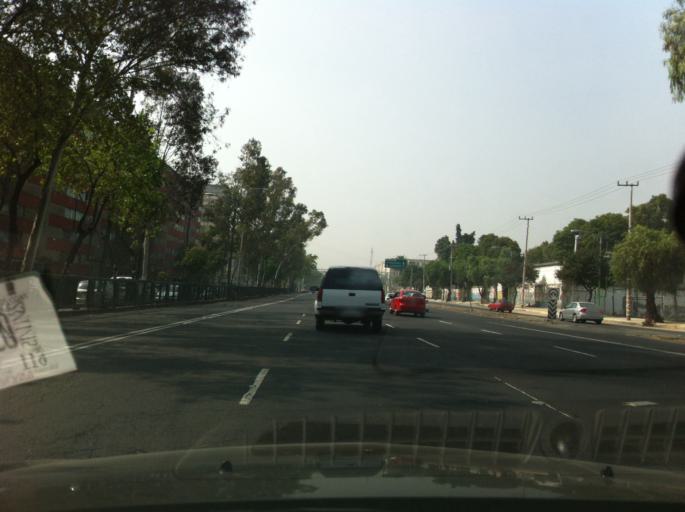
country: MX
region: Mexico City
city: Cuauhtemoc
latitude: 19.4553
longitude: -99.1408
